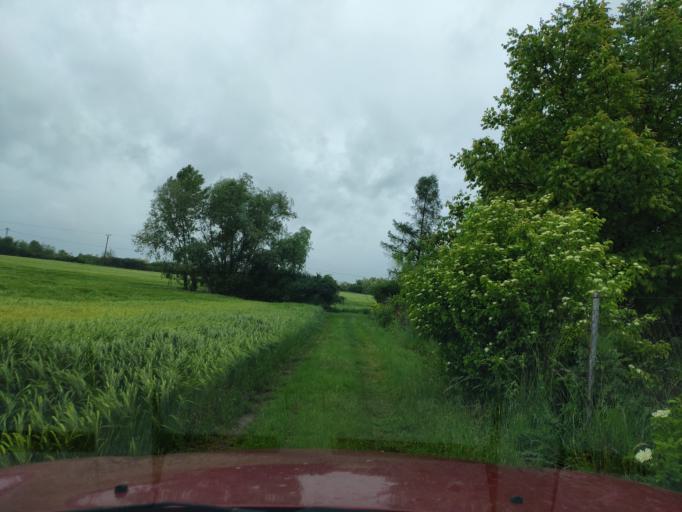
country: SK
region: Kosicky
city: Cierna nad Tisou
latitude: 48.4270
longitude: 22.0920
